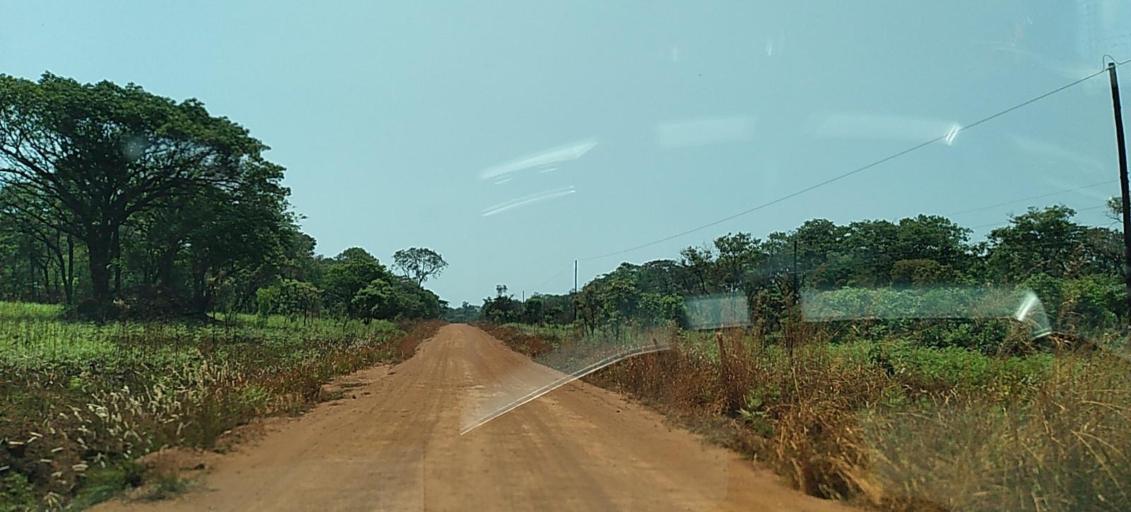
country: CD
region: Katanga
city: Kipushi
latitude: -11.9847
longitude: 26.8666
